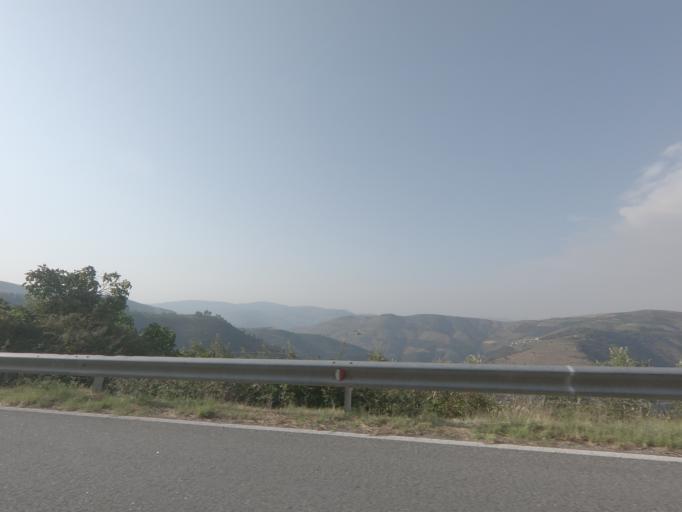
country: PT
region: Viseu
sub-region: Tabuaco
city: Tabuaco
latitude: 41.1199
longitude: -7.5637
